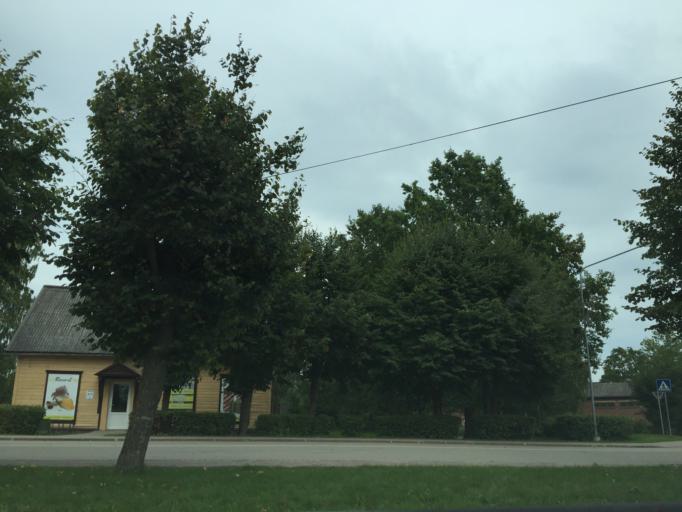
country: LV
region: Zilupes
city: Zilupe
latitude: 56.3888
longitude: 28.1210
